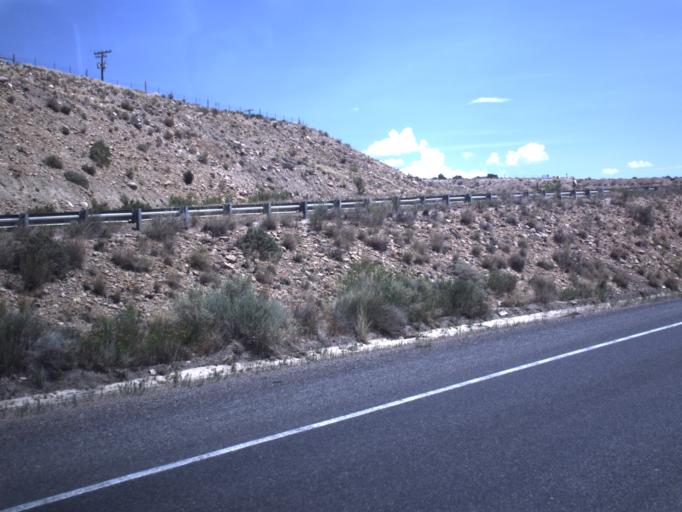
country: US
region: Utah
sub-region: Emery County
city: Huntington
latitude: 39.3733
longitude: -111.0628
